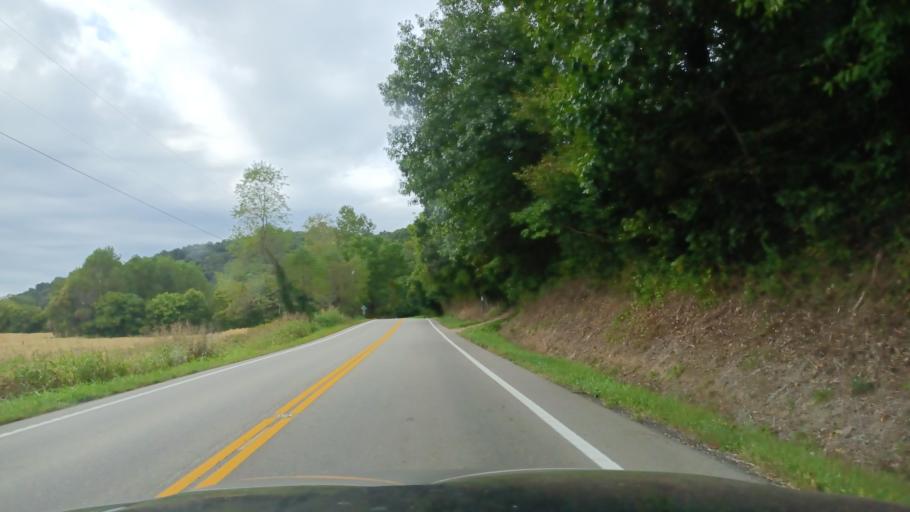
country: US
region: Ohio
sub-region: Vinton County
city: McArthur
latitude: 39.2705
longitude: -82.6413
